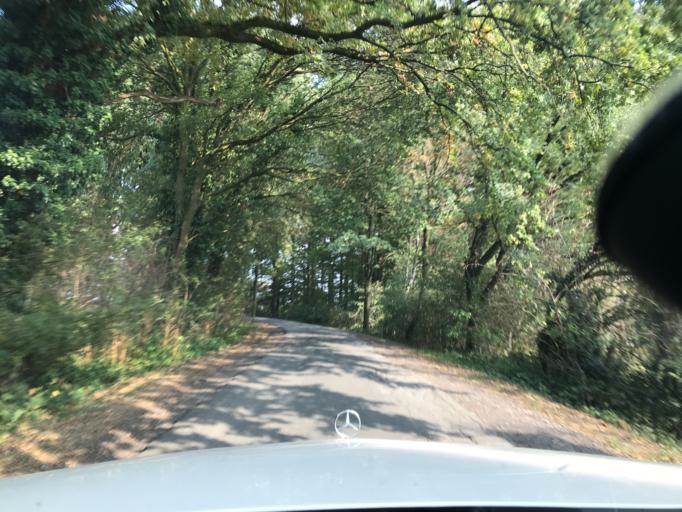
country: DE
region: North Rhine-Westphalia
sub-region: Regierungsbezirk Arnsberg
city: Werl
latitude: 51.6121
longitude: 7.8672
